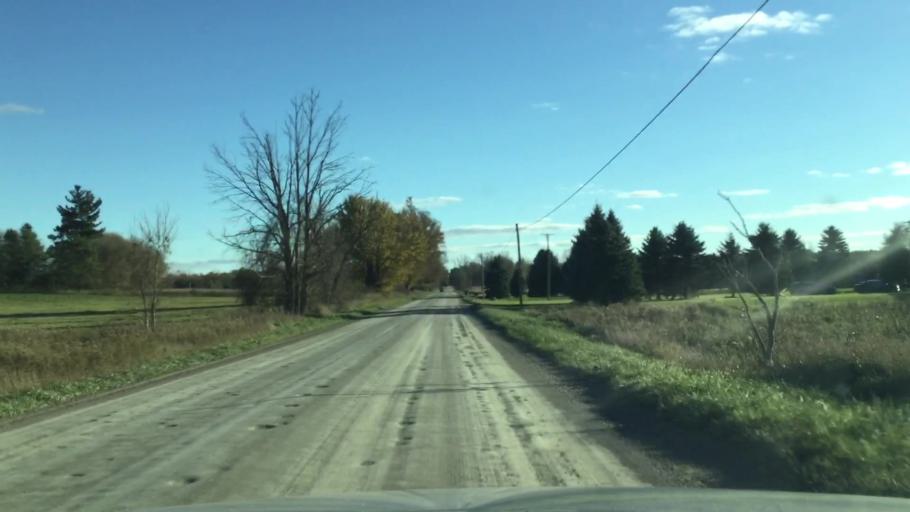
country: US
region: Michigan
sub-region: Lapeer County
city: Lapeer
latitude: 43.0657
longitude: -83.2270
